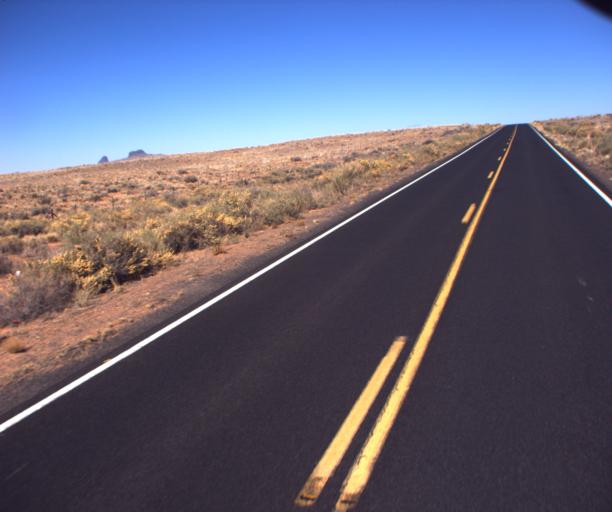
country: US
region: Arizona
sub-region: Navajo County
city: Dilkon
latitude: 35.3609
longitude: -110.4246
